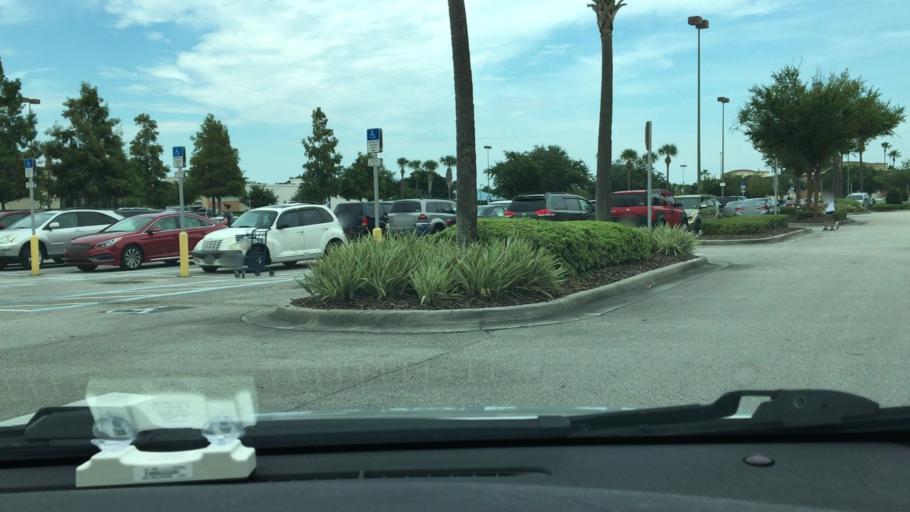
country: US
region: Florida
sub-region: Seminole County
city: Lake Mary
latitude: 28.7988
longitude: -81.3346
